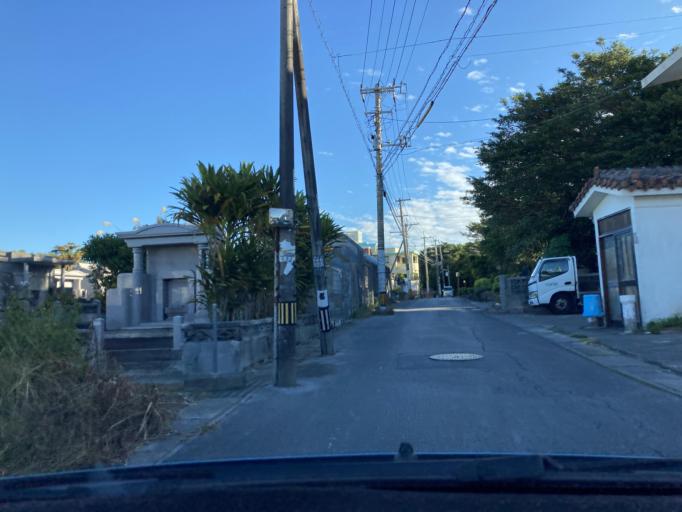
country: JP
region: Okinawa
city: Naha-shi
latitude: 26.2037
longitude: 127.7132
